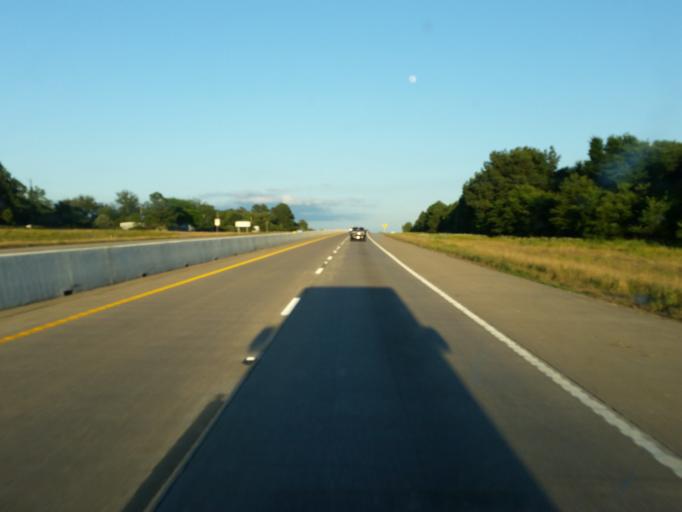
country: US
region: Texas
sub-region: Van Zandt County
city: Wills Point
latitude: 32.6123
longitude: -95.9626
